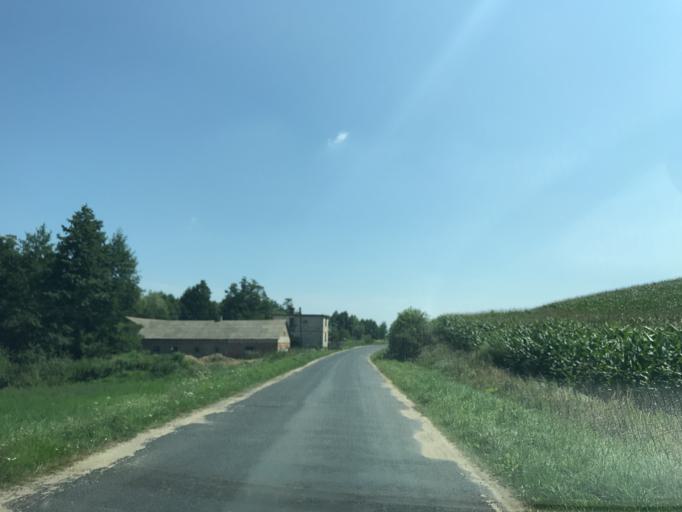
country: PL
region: Kujawsko-Pomorskie
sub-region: Powiat golubsko-dobrzynski
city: Zbojno
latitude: 52.9977
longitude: 19.2085
